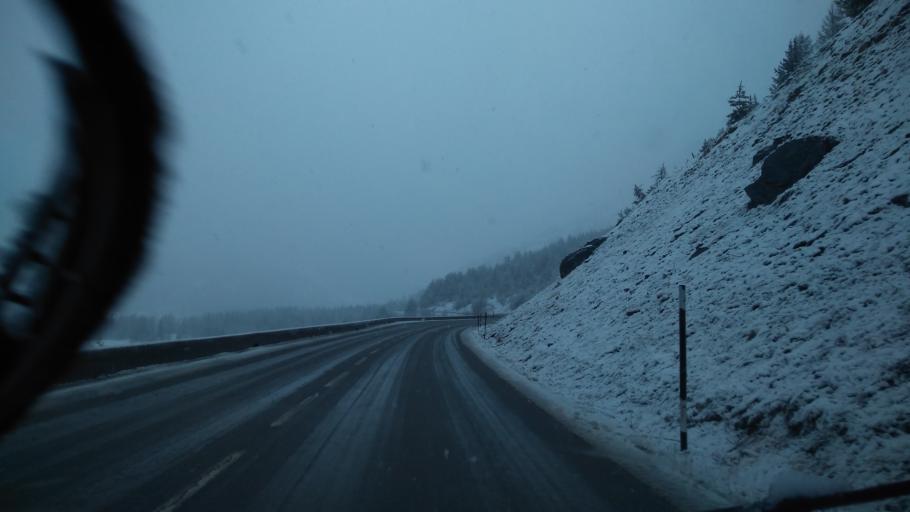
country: FR
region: Provence-Alpes-Cote d'Azur
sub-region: Departement des Hautes-Alpes
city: Le Monetier-les-Bains
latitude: 44.9848
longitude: 6.4959
